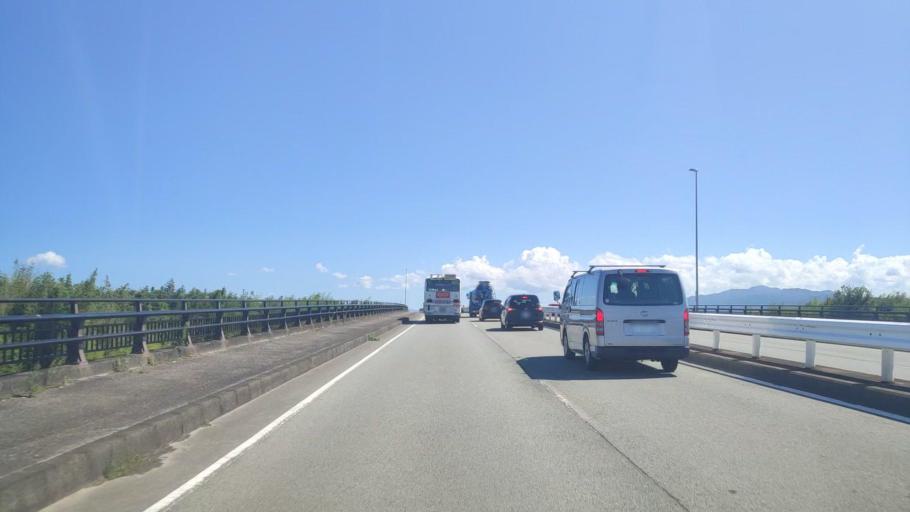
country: JP
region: Mie
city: Hisai-motomachi
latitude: 34.6494
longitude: 136.5193
